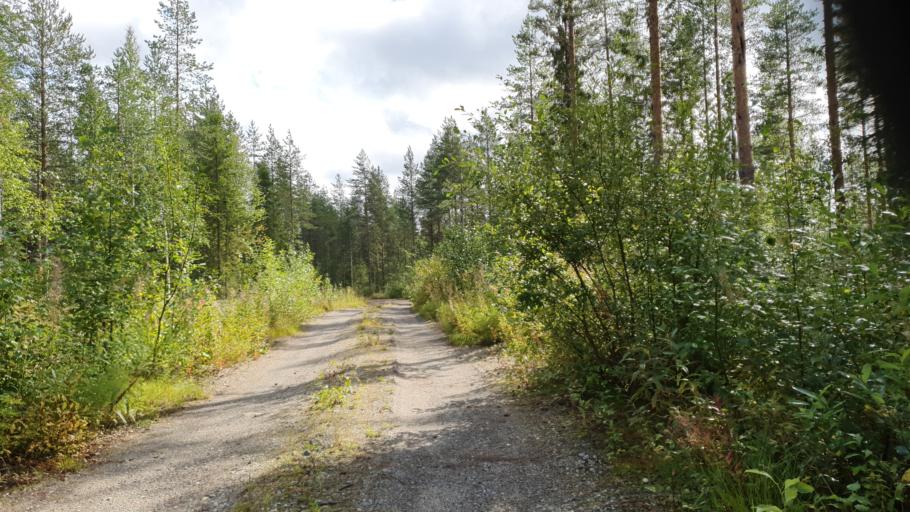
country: FI
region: Kainuu
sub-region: Kehys-Kainuu
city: Kuhmo
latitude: 64.1401
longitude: 29.3886
